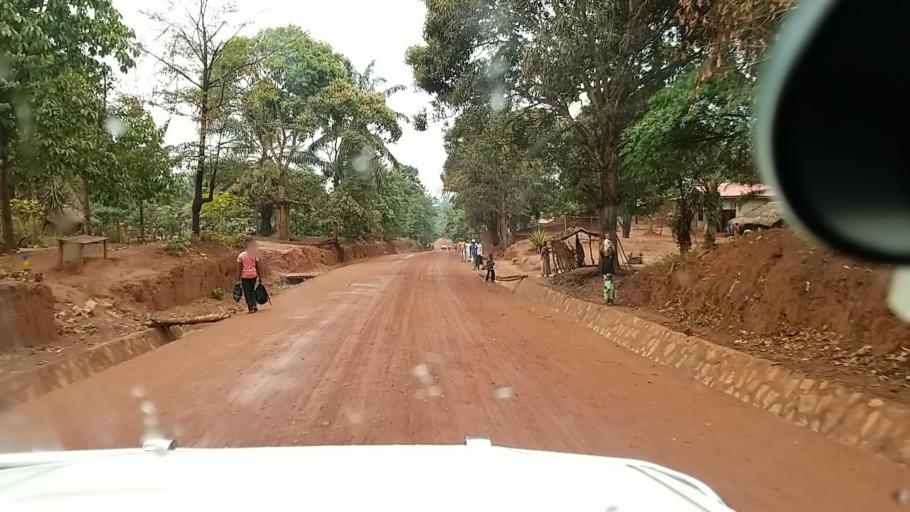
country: CD
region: Equateur
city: Gemena
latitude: 3.2291
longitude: 19.7774
